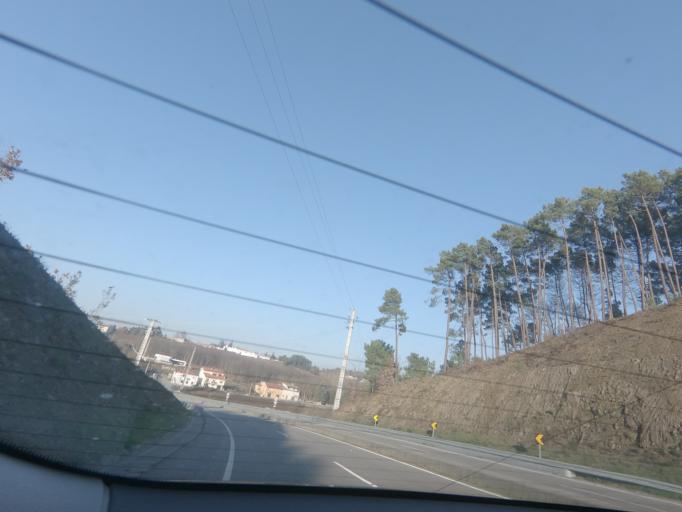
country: PT
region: Vila Real
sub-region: Vila Real
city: Vila Real
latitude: 41.2884
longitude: -7.7225
